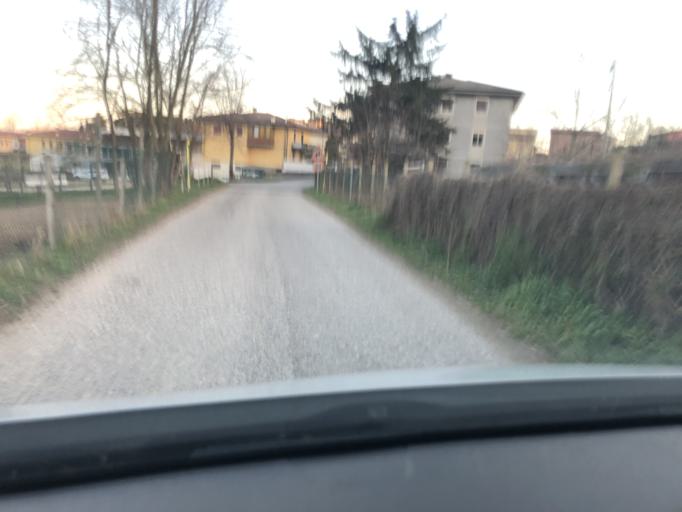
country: IT
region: Veneto
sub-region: Provincia di Verona
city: Sandra
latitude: 45.4577
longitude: 10.8141
